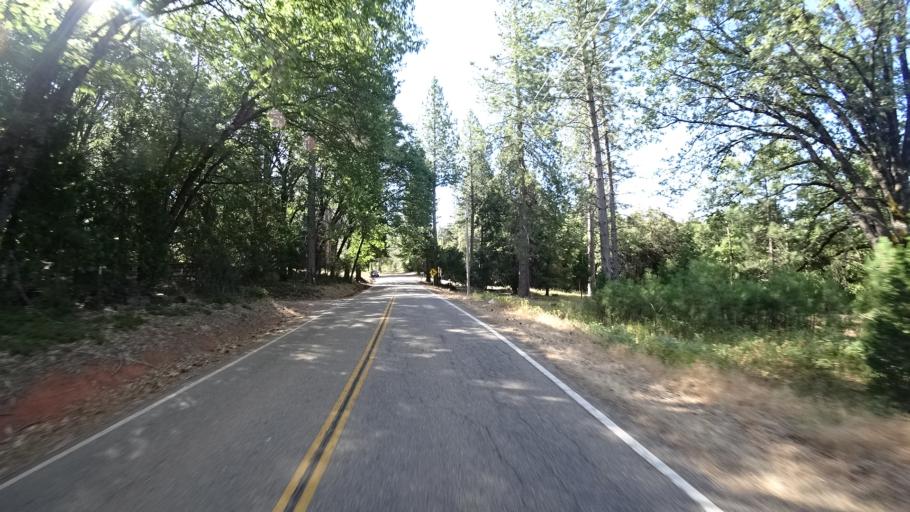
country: US
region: California
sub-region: Amador County
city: Pioneer
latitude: 38.3823
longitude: -120.5251
